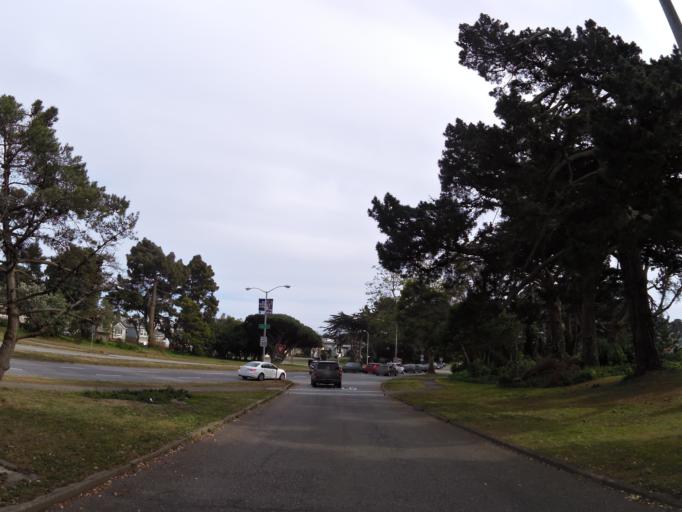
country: US
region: California
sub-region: San Mateo County
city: Daly City
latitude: 37.7328
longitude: -122.4942
